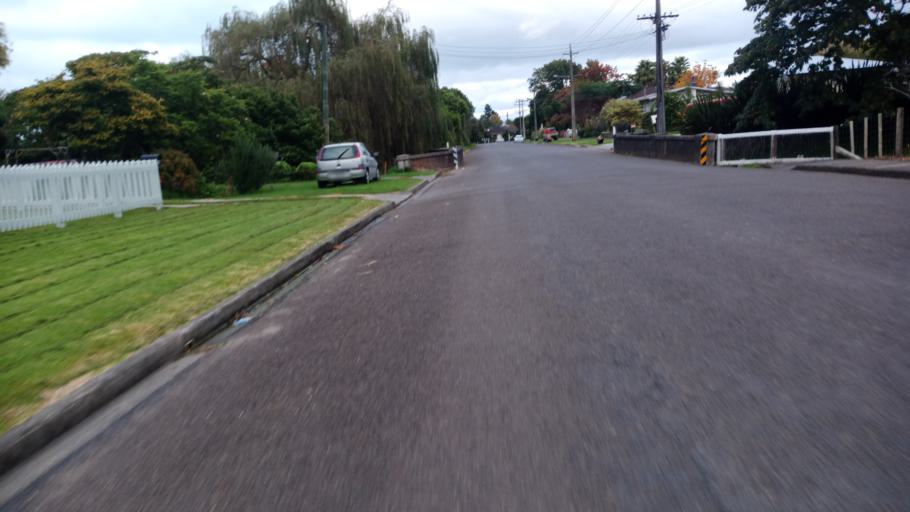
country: NZ
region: Gisborne
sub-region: Gisborne District
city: Gisborne
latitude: -38.6463
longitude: 178.0239
